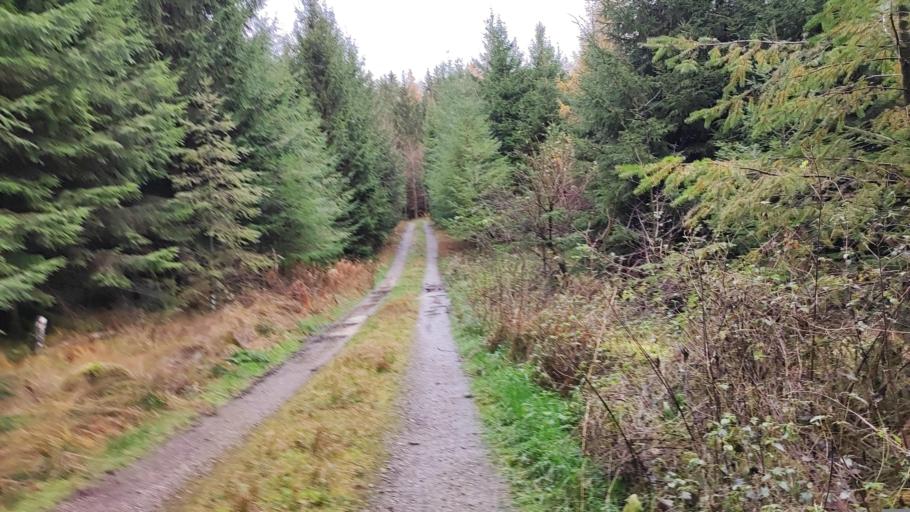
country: DE
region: Bavaria
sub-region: Swabia
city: Ziemetshausen
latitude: 48.3351
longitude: 10.5199
